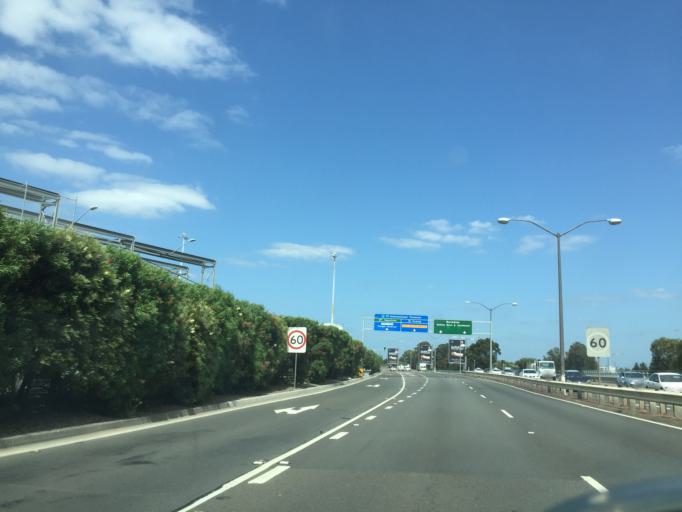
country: AU
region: New South Wales
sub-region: Rockdale
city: Arncliffe
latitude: -33.9288
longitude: 151.1666
